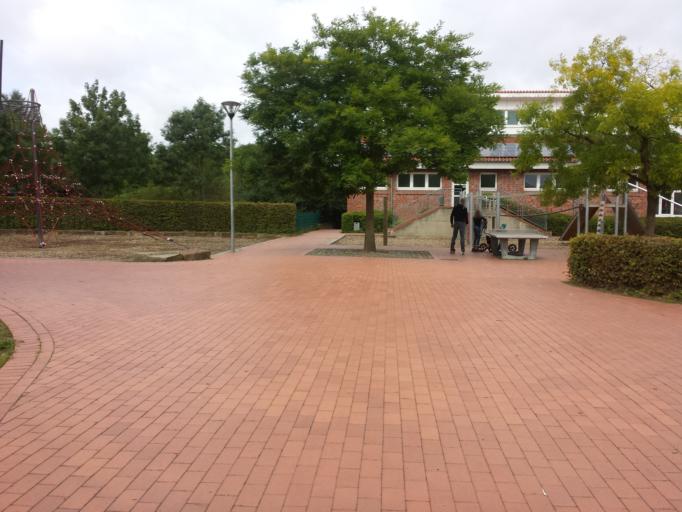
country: DE
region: North Rhine-Westphalia
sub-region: Regierungsbezirk Detmold
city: Guetersloh
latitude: 51.8876
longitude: 8.3949
